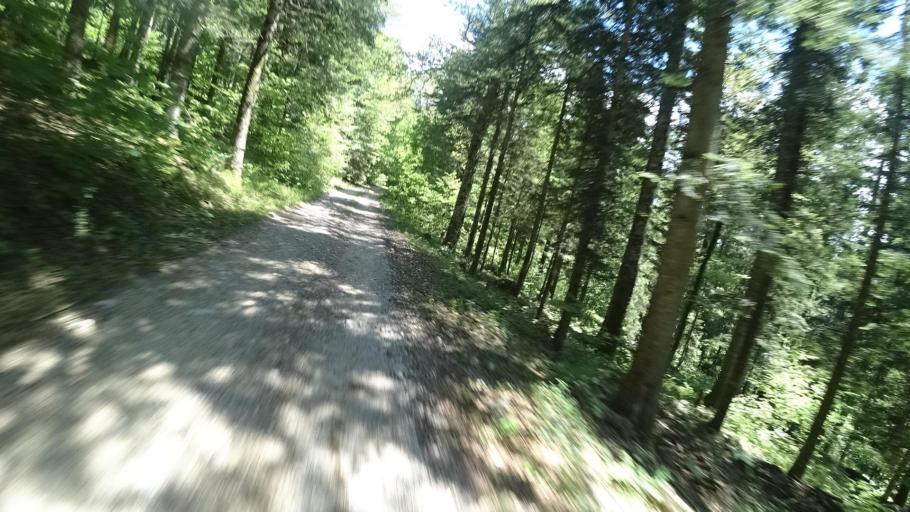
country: BA
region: Federation of Bosnia and Herzegovina
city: Bosanska Krupa
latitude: 44.8091
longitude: 16.0533
